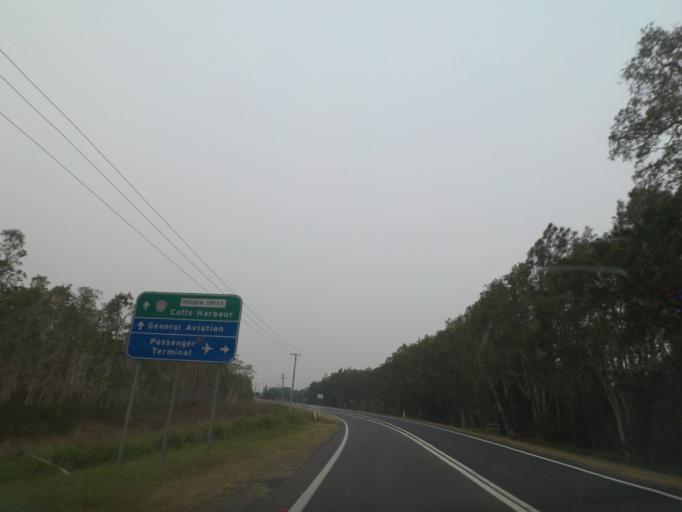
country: AU
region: New South Wales
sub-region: Coffs Harbour
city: Coffs Harbour
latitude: -30.3188
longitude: 153.1088
